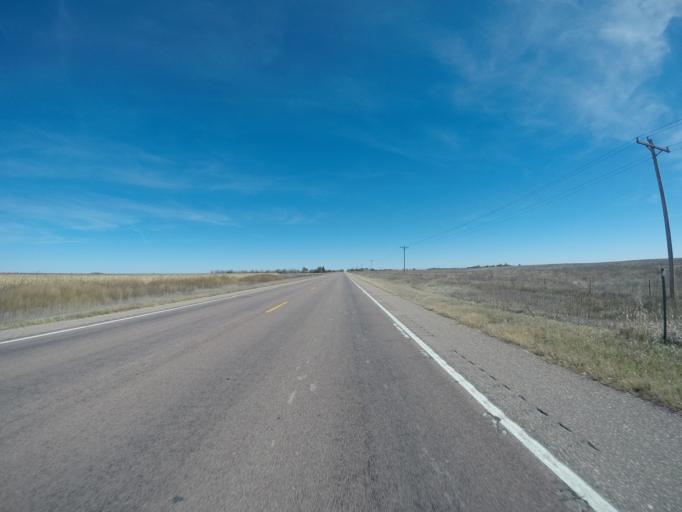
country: US
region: Colorado
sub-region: Yuma County
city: Yuma
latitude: 39.6559
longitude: -102.7032
